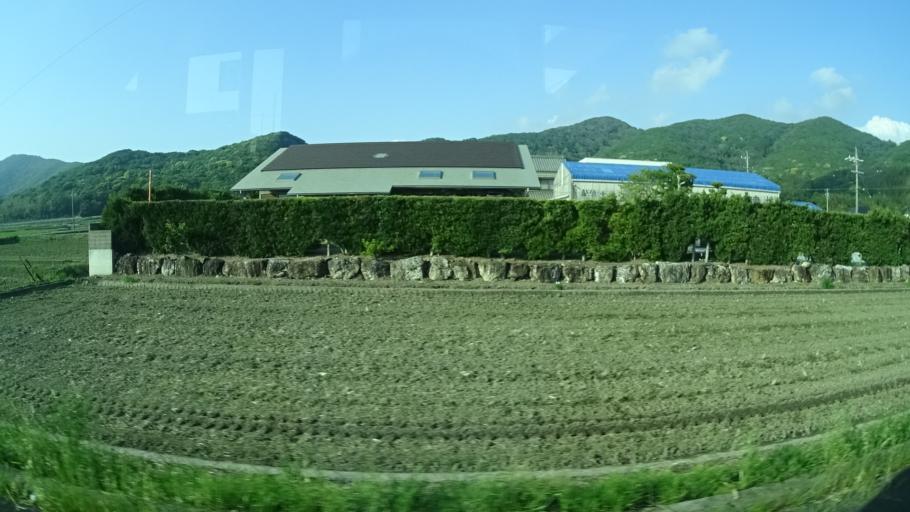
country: JP
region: Aichi
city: Tahara
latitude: 34.6534
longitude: 137.2147
